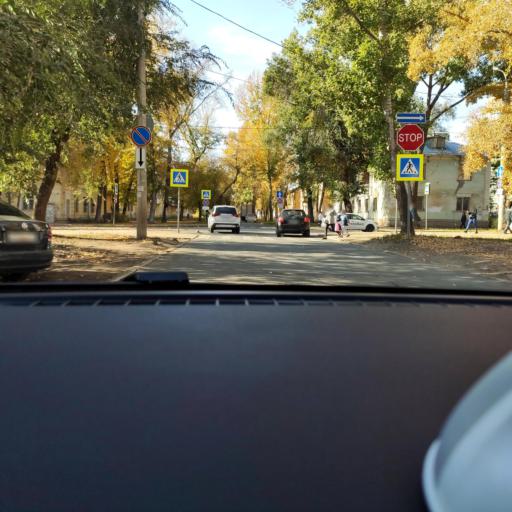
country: RU
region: Samara
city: Samara
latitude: 53.2182
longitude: 50.2511
